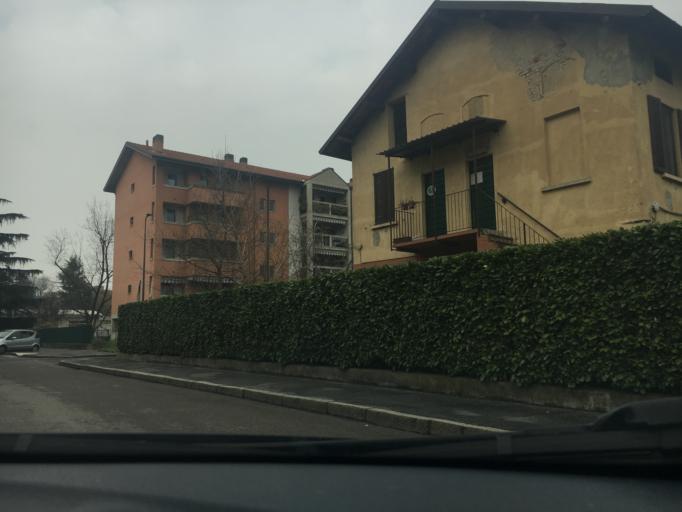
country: IT
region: Lombardy
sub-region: Citta metropolitana di Milano
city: Pero
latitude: 45.4905
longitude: 9.1038
